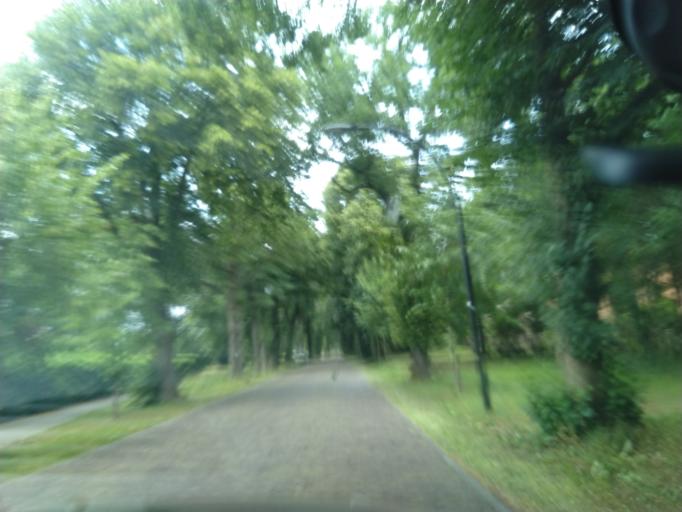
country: NL
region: Groningen
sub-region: Gemeente Vlagtwedde
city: Vlagtwedde
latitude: 53.0885
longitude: 7.1358
